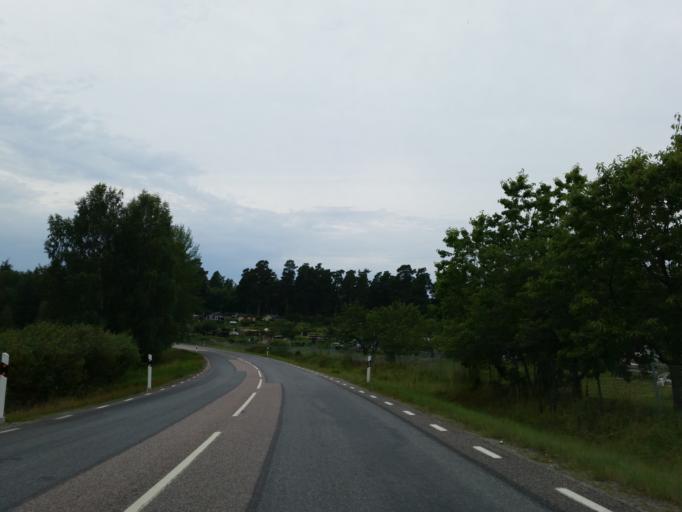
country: SE
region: Stockholm
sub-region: Sodertalje Kommun
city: Soedertaelje
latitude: 59.2022
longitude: 17.5666
